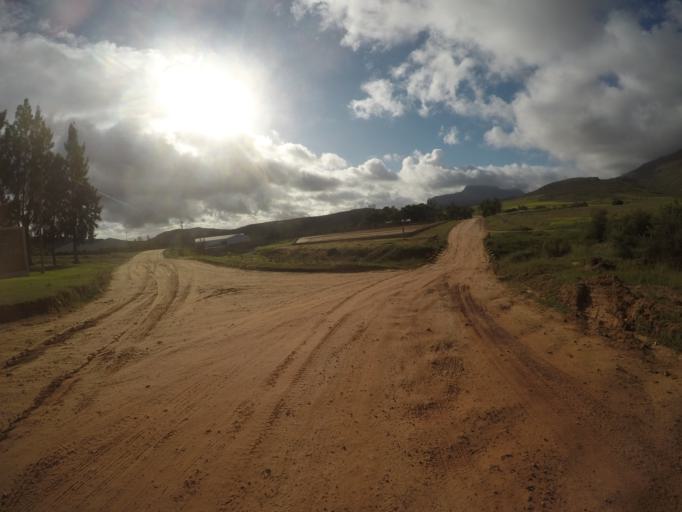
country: ZA
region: Western Cape
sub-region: West Coast District Municipality
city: Clanwilliam
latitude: -32.3420
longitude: 18.8319
